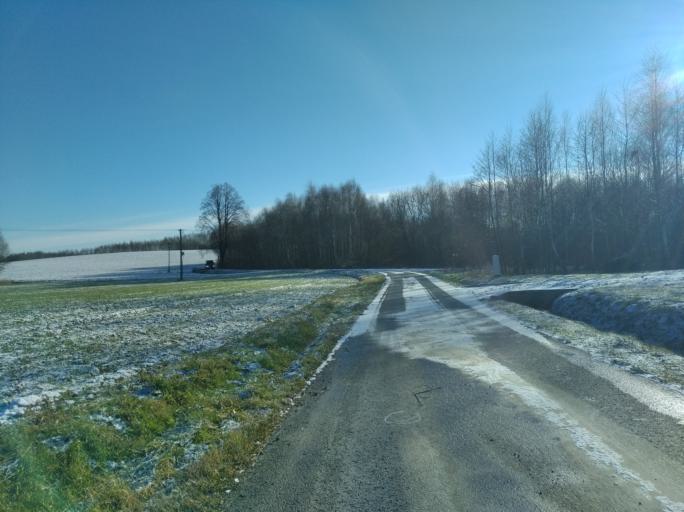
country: PL
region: Subcarpathian Voivodeship
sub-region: Powiat strzyzowski
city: Czudec
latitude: 49.9476
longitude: 21.7640
